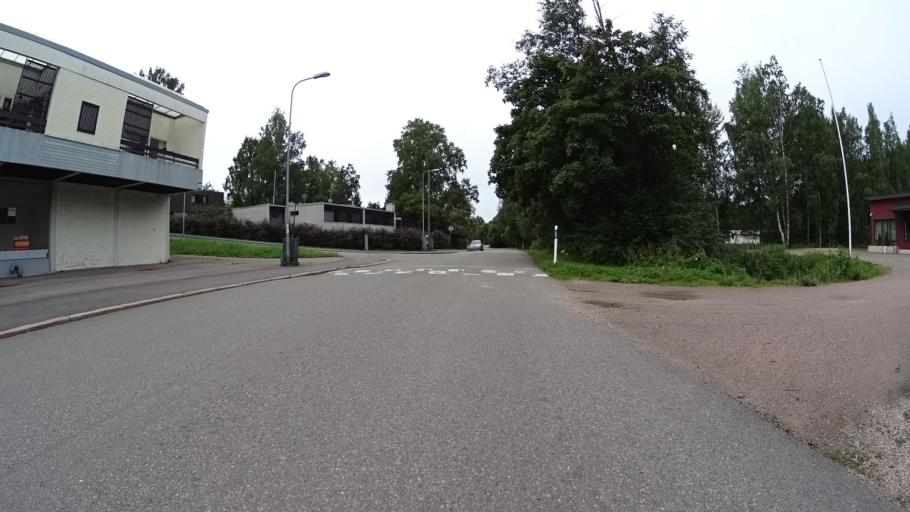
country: FI
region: Uusimaa
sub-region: Helsinki
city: Helsinki
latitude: 60.2234
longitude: 24.9385
